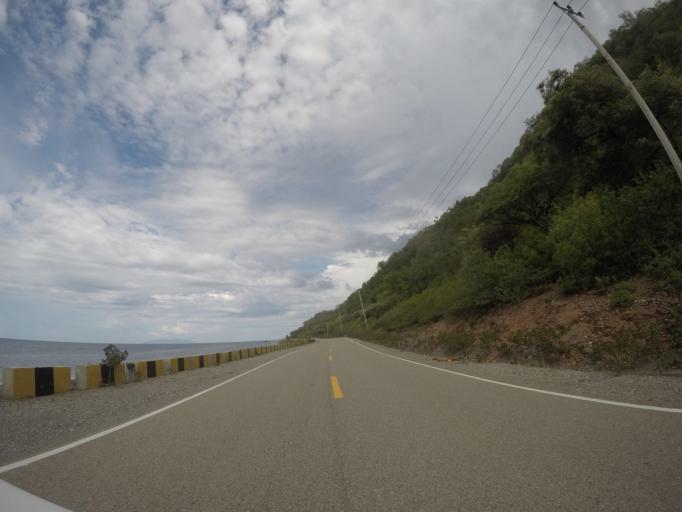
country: TL
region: Liquica
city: Maubara
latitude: -8.6157
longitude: 125.1848
